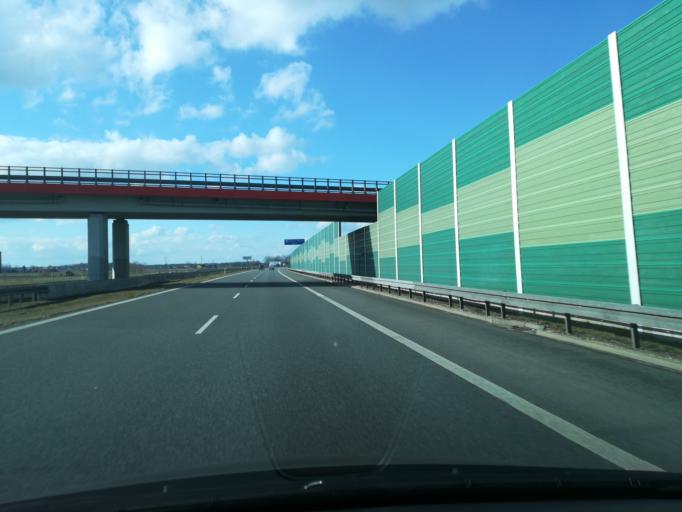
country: PL
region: Lodz Voivodeship
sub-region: Powiat kutnowski
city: Strzelce
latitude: 52.2683
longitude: 19.4244
